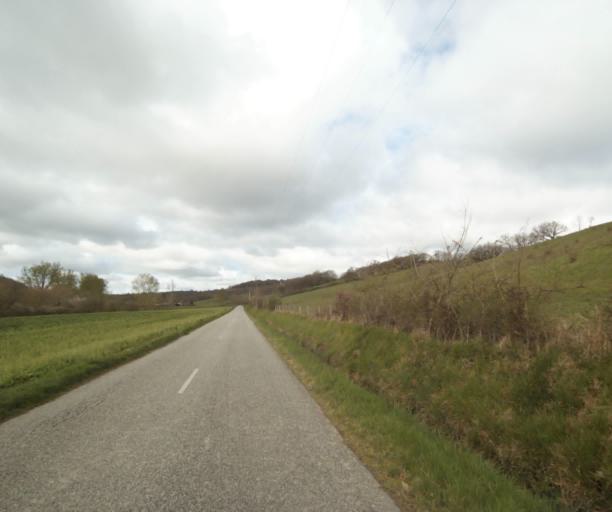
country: FR
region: Midi-Pyrenees
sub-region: Departement de l'Ariege
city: Saverdun
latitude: 43.2265
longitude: 1.5442
